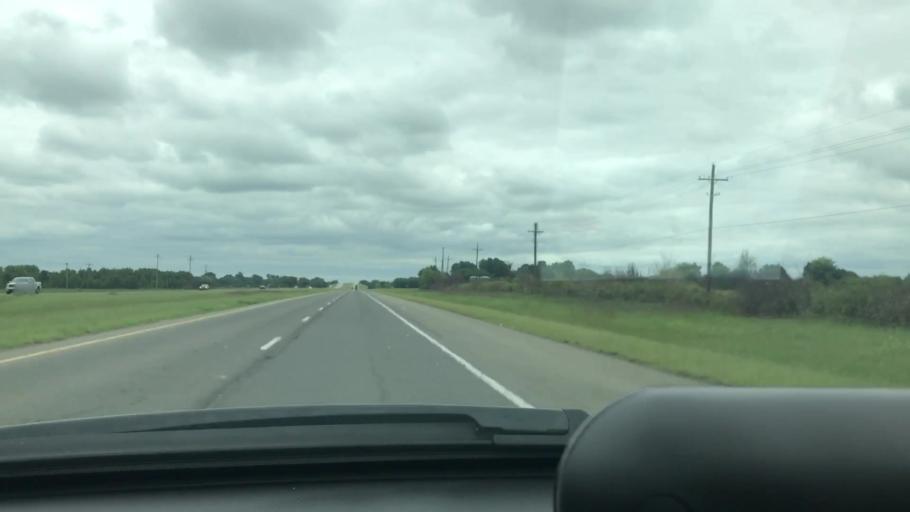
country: US
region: Oklahoma
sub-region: Wagoner County
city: Wagoner
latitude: 35.8641
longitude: -95.4025
